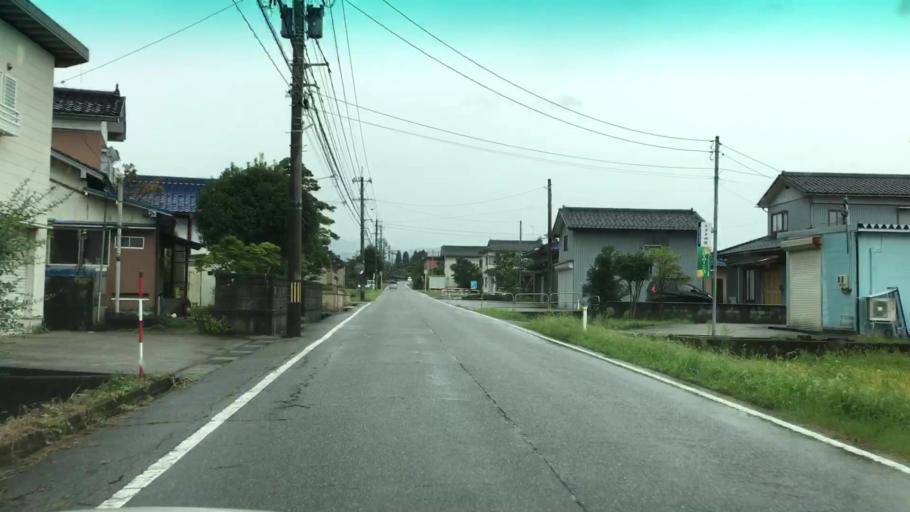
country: JP
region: Toyama
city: Kamiichi
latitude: 36.6446
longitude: 137.3202
